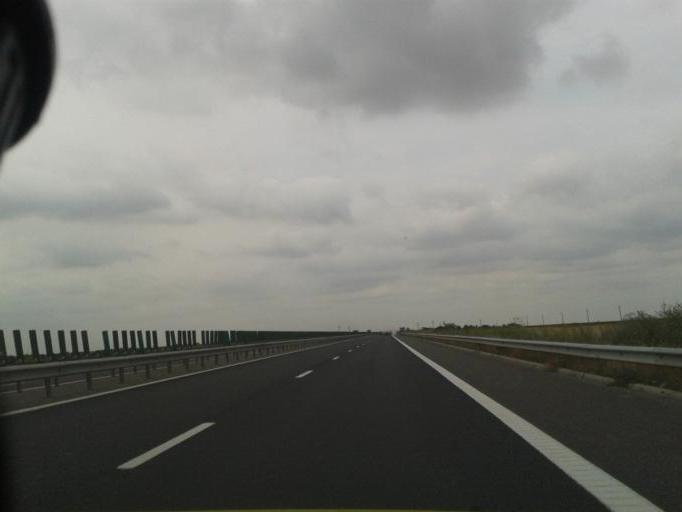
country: RO
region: Calarasi
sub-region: Comuna Perisoru
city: Perisoru
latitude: 44.3965
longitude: 27.4927
